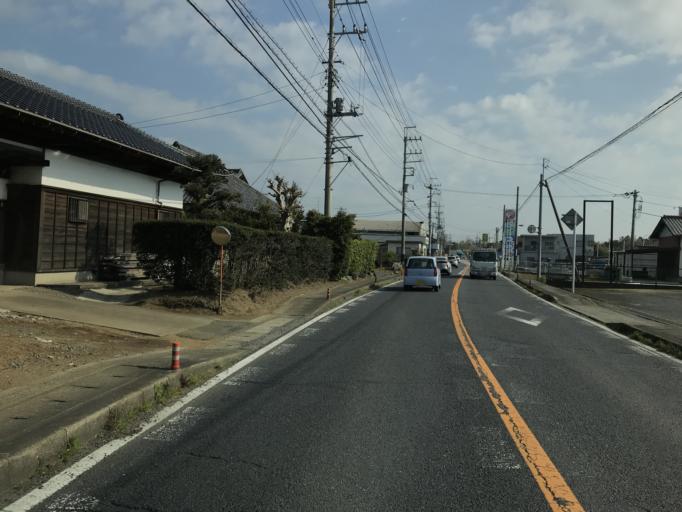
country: JP
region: Chiba
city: Sawara
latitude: 35.8277
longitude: 140.4116
